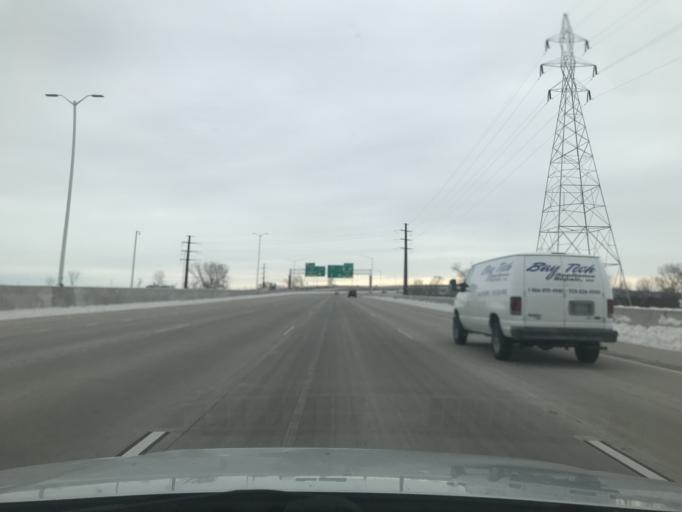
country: US
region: Wisconsin
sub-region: Brown County
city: Howard
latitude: 44.5732
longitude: -88.0487
